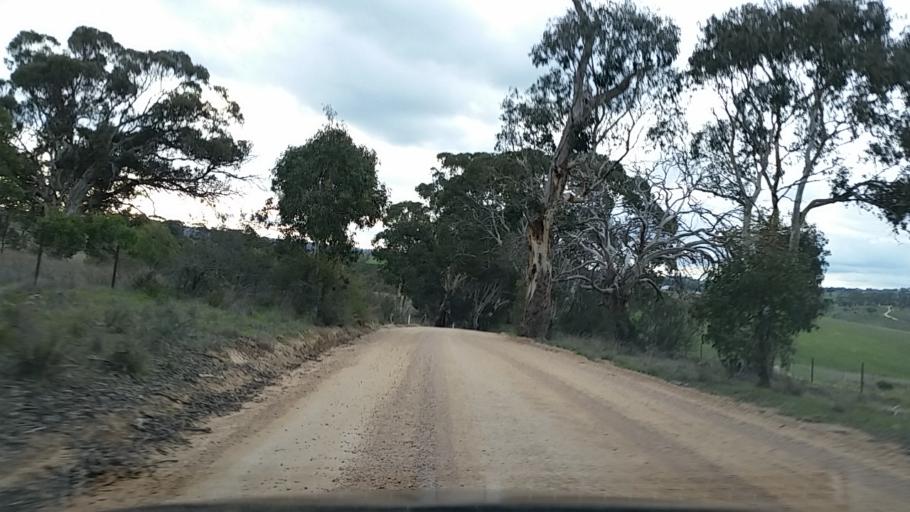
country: AU
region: South Australia
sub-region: Mount Barker
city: Nairne
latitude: -34.9620
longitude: 139.0233
